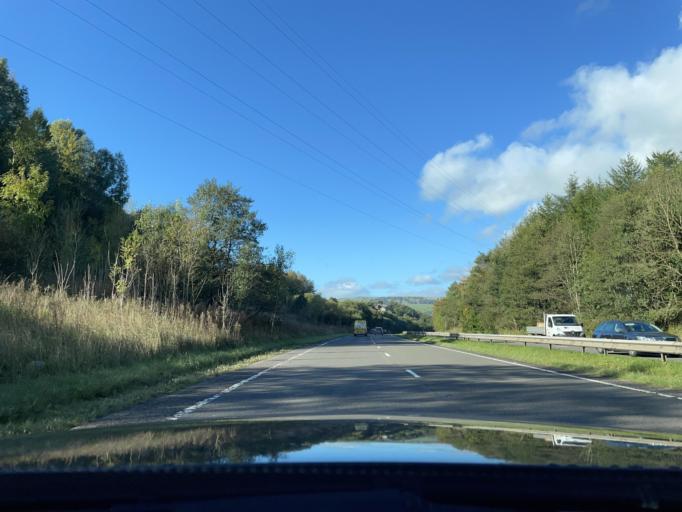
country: GB
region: England
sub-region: Derbyshire
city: Chinley
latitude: 53.3339
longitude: -1.9467
